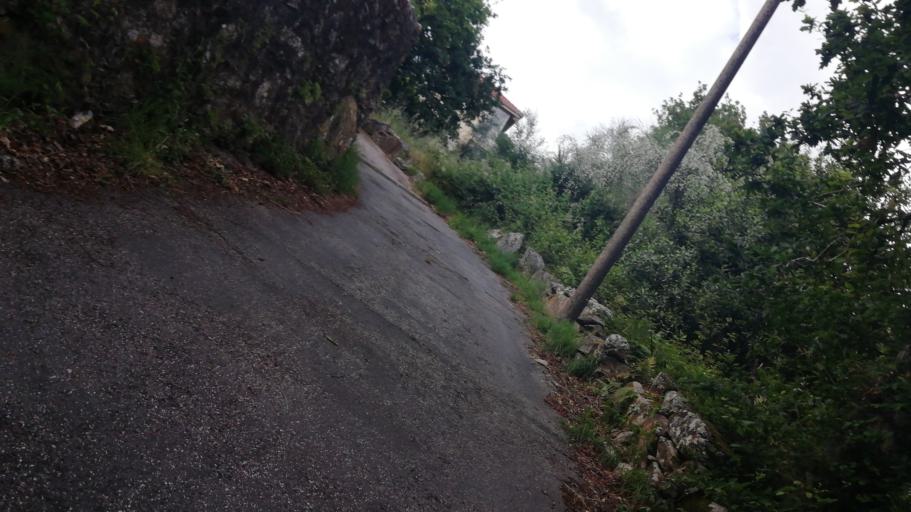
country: ES
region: Galicia
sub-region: Provincia de Pontevedra
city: A Guarda
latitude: 41.8846
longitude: -8.8605
